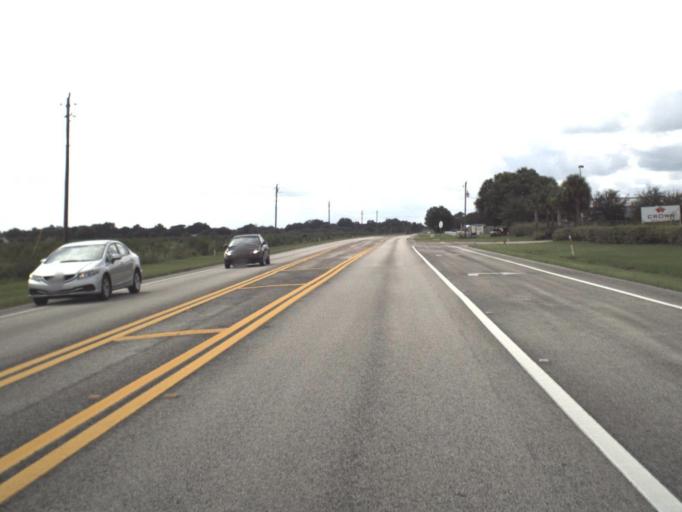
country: US
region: Florida
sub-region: DeSoto County
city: Nocatee
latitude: 27.2015
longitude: -81.9413
